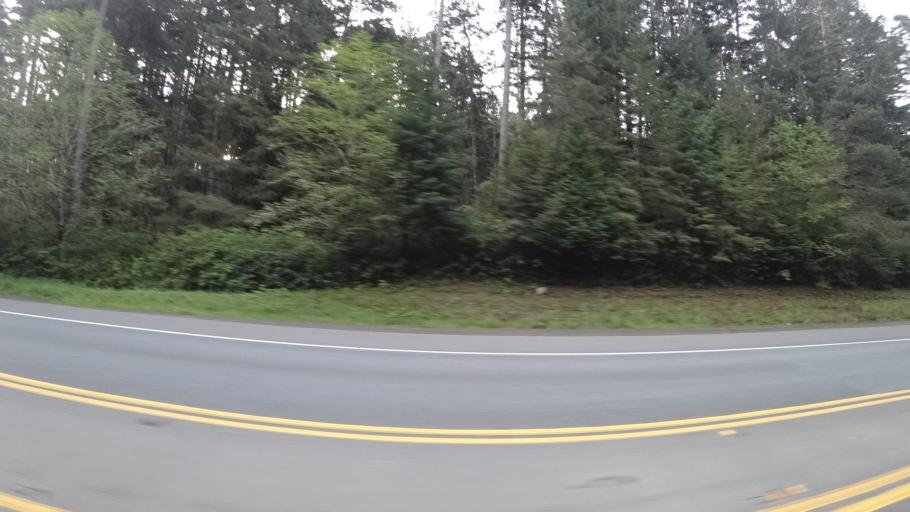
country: US
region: Oregon
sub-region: Coos County
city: Lakeside
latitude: 43.5630
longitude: -124.2054
